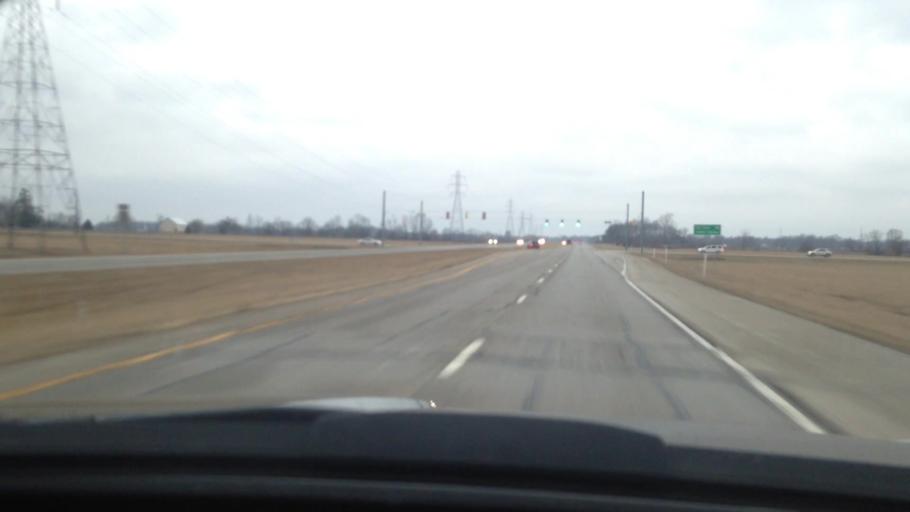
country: US
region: Indiana
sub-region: Delaware County
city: Muncie
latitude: 40.1419
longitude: -85.4037
